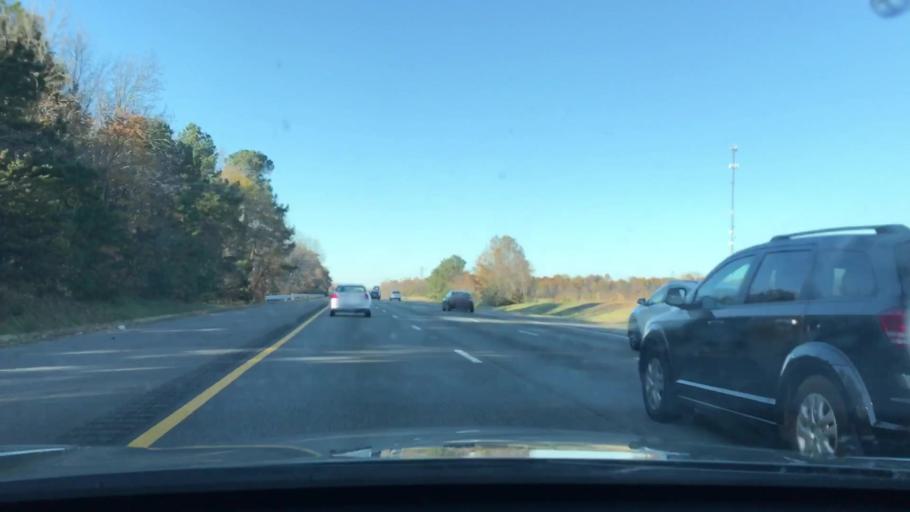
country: US
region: Virginia
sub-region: Spotsylvania County
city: Spotsylvania Courthouse
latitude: 38.0755
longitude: -77.5117
